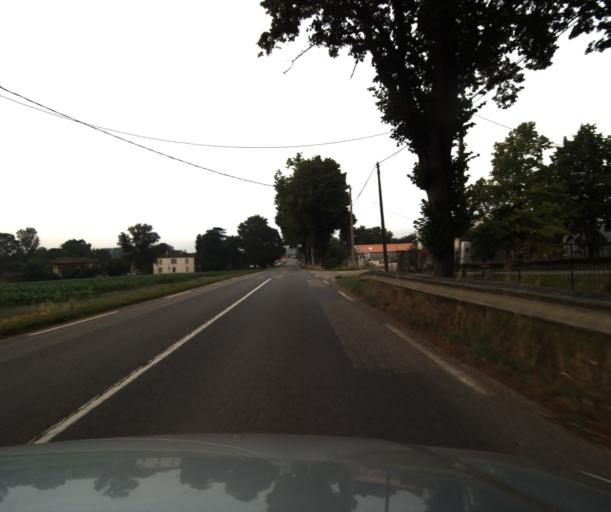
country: FR
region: Midi-Pyrenees
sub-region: Departement du Tarn-et-Garonne
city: Beaumont-de-Lomagne
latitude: 43.8101
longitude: 0.9012
